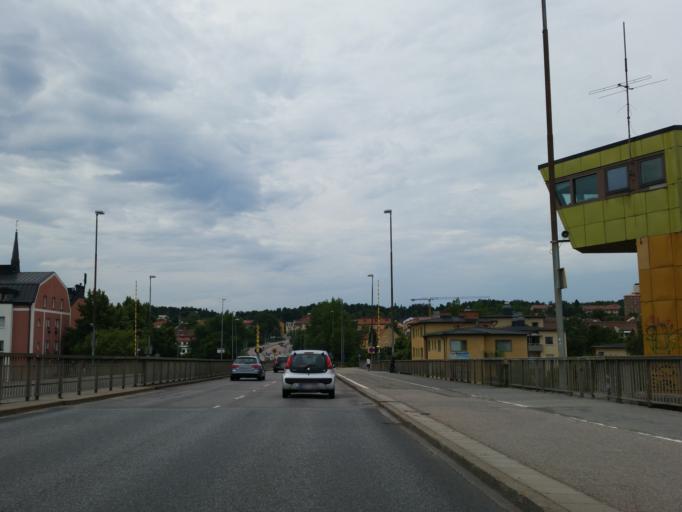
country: SE
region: Stockholm
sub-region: Sodertalje Kommun
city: Soedertaelje
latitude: 59.2002
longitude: 17.6289
